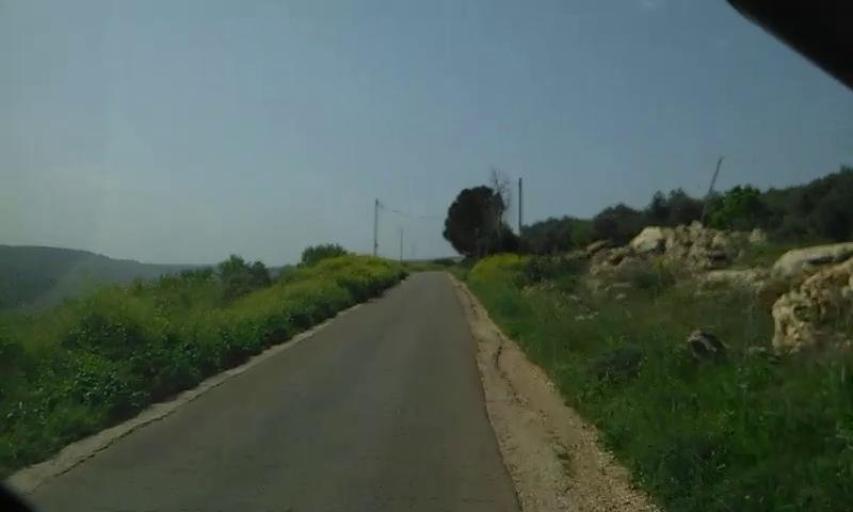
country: PS
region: West Bank
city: `Anin
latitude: 32.4982
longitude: 35.1797
